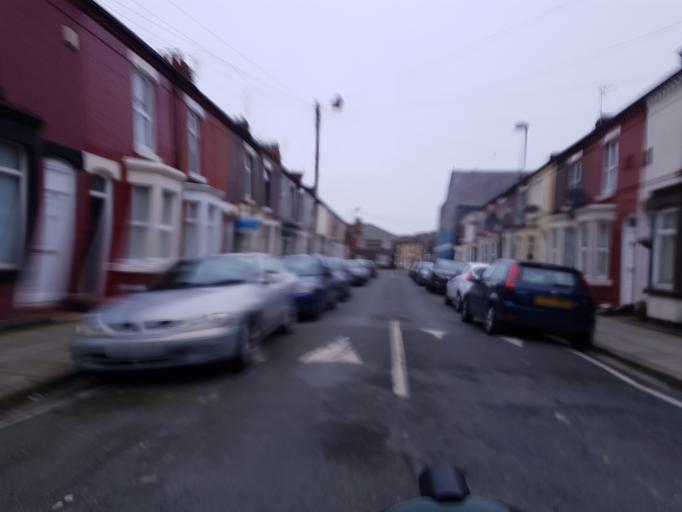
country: GB
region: England
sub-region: Liverpool
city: Liverpool
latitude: 53.4407
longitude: -2.9654
